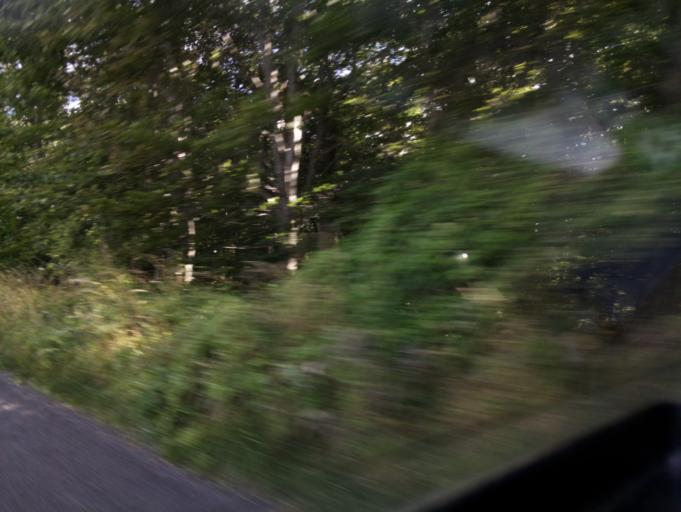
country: GB
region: England
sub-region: Gloucestershire
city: Cirencester
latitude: 51.7441
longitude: -1.9943
